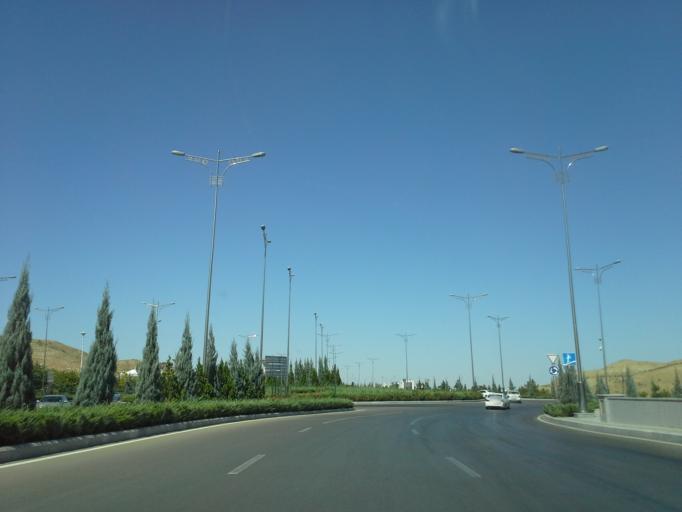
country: TM
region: Ahal
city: Ashgabat
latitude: 37.9312
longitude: 58.3180
